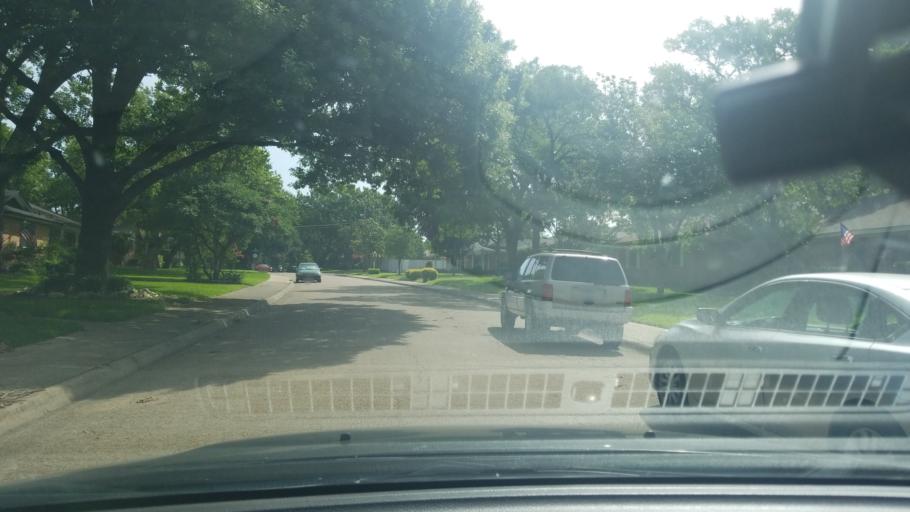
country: US
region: Texas
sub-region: Dallas County
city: Highland Park
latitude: 32.8017
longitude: -96.6969
